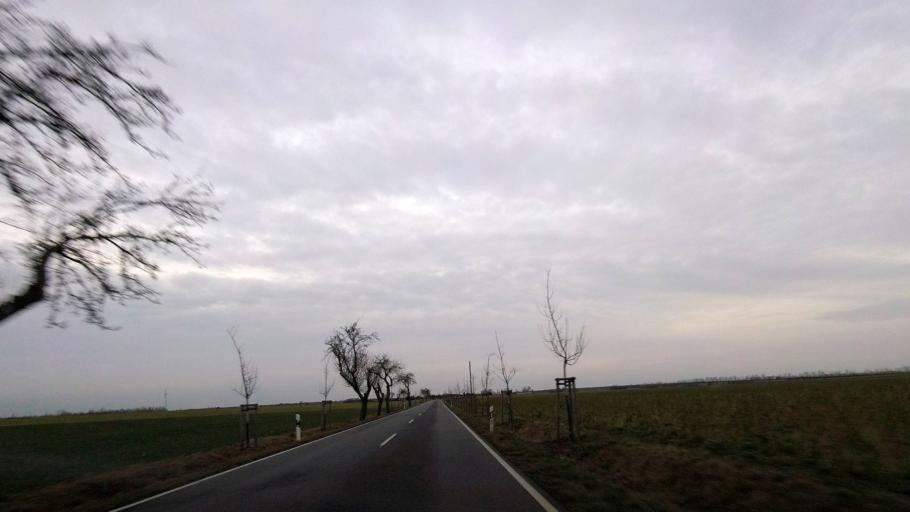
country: DE
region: Brandenburg
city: Niedergorsdorf
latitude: 51.9420
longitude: 12.9781
